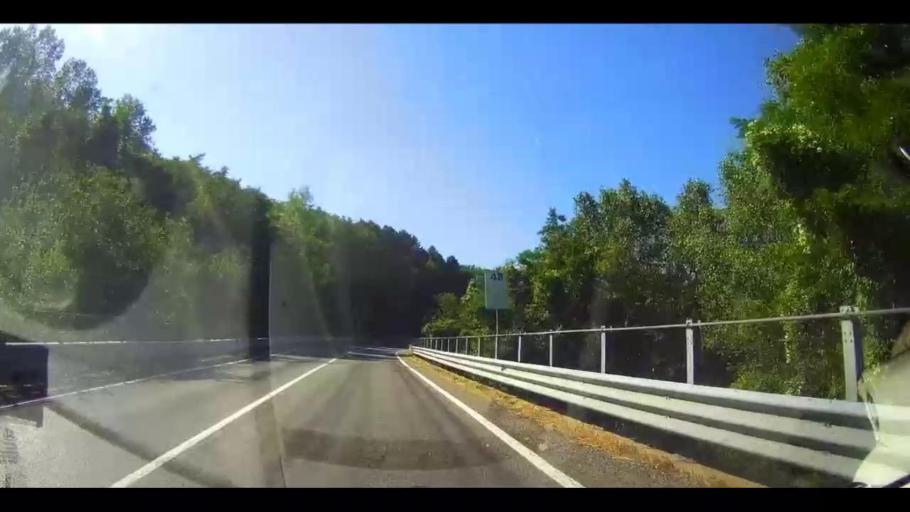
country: IT
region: Calabria
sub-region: Provincia di Cosenza
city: Spezzano Piccolo
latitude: 39.2988
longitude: 16.3557
